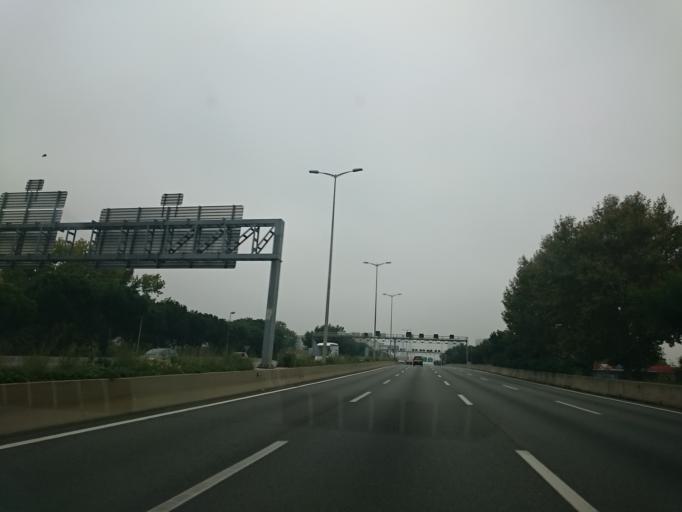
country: ES
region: Catalonia
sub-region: Provincia de Barcelona
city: L'Hospitalet de Llobregat
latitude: 41.3460
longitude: 2.1104
